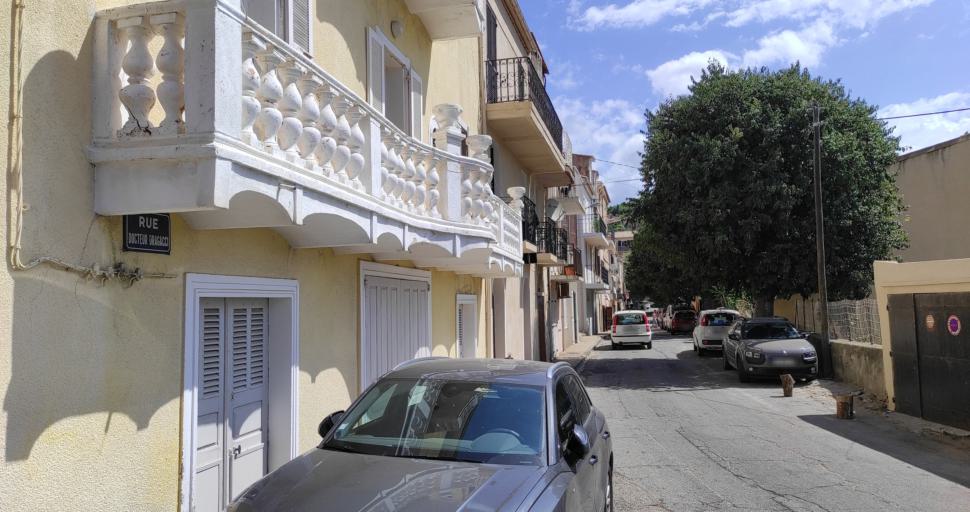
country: FR
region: Corsica
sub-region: Departement de la Corse-du-Sud
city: Cargese
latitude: 42.1342
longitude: 8.5947
